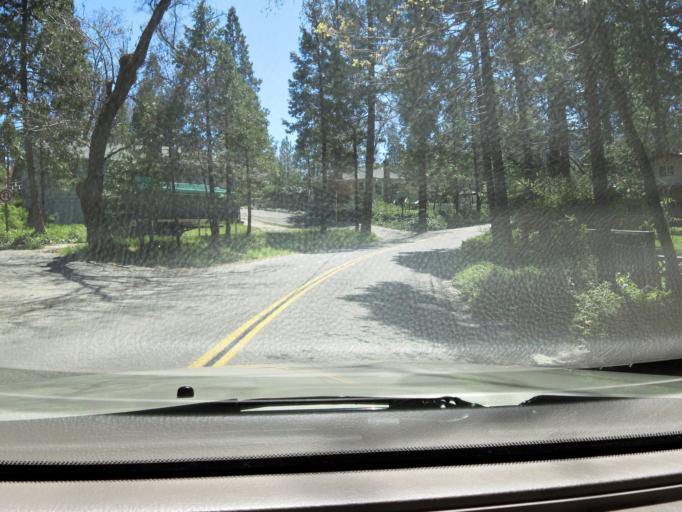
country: US
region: California
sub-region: Madera County
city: Oakhurst
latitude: 37.3241
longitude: -119.5663
